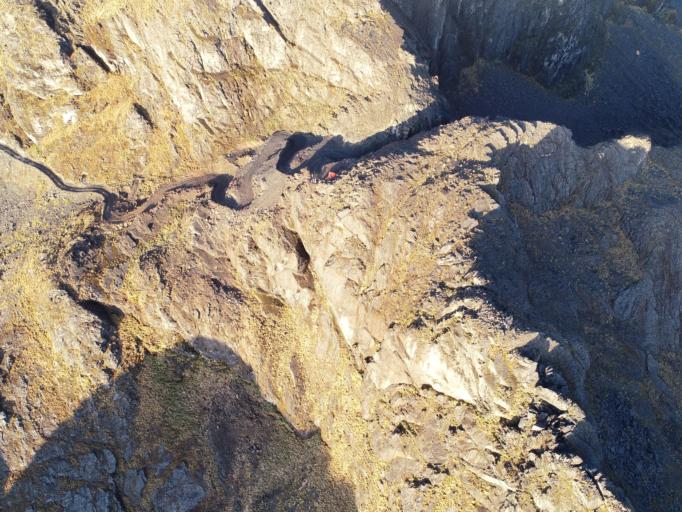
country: PE
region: Puno
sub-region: San Antonio De Putina
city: Sina
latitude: -14.7360
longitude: -69.0488
